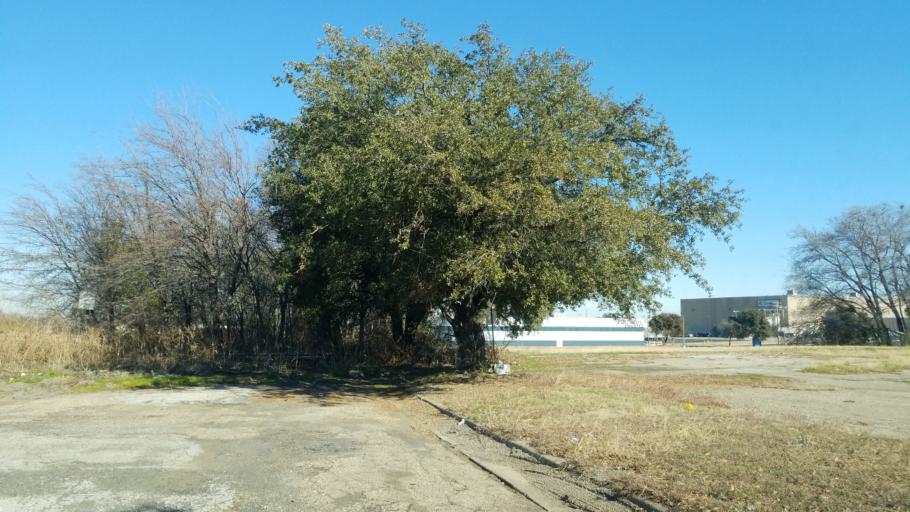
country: US
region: Texas
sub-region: Dallas County
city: Grand Prairie
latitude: 32.7415
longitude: -97.0523
